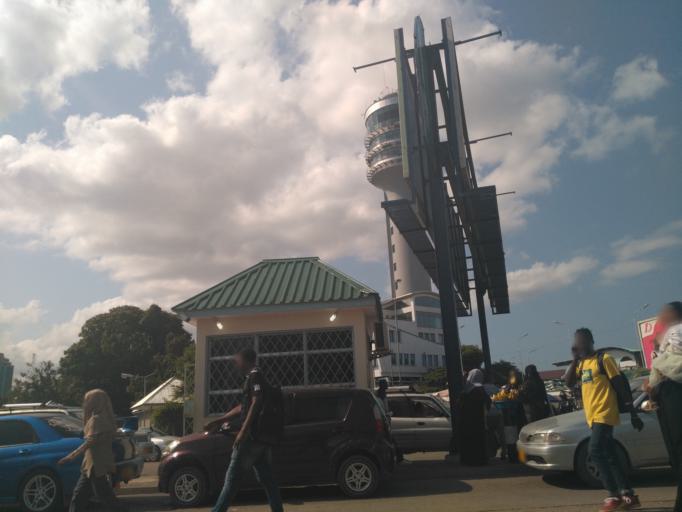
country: TZ
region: Dar es Salaam
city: Dar es Salaam
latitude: -6.8202
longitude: 39.2983
